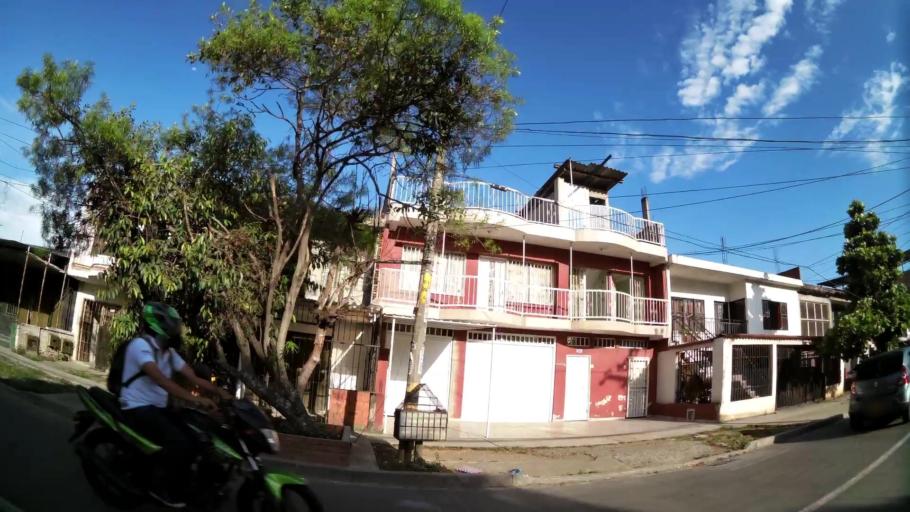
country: CO
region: Valle del Cauca
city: Cali
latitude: 3.4335
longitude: -76.5174
